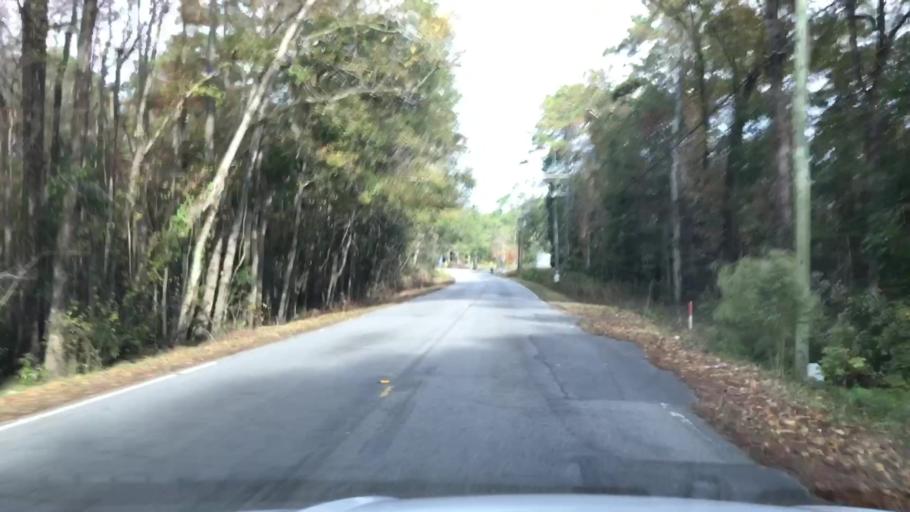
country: US
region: South Carolina
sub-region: Charleston County
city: Ravenel
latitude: 32.7723
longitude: -80.2443
